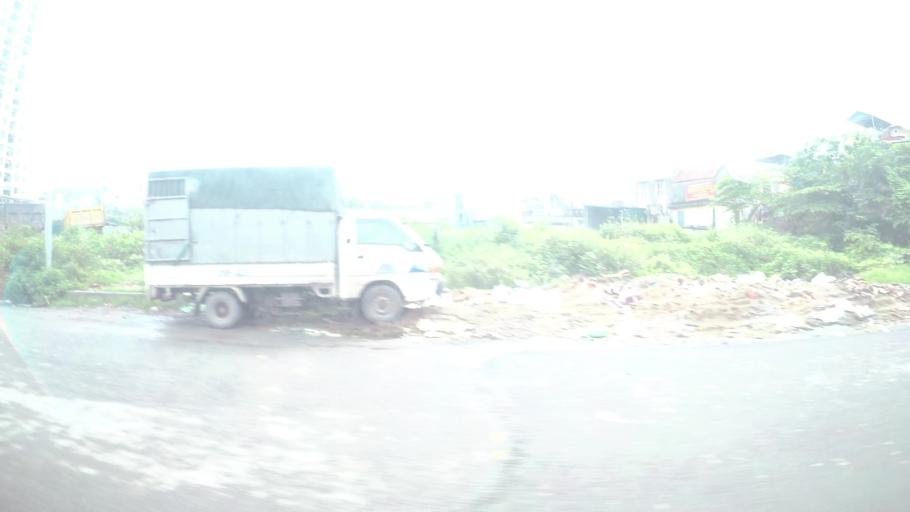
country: VN
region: Ha Noi
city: Van Dien
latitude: 20.9664
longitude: 105.8683
